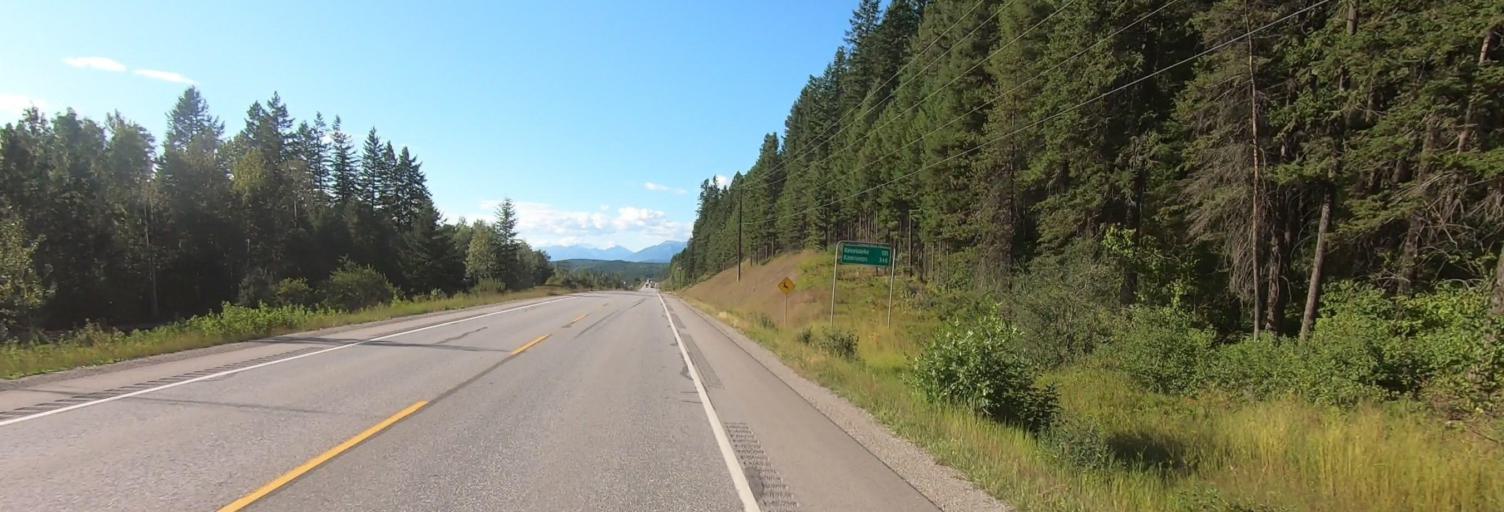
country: CA
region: British Columbia
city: Golden
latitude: 51.4108
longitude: -117.0450
